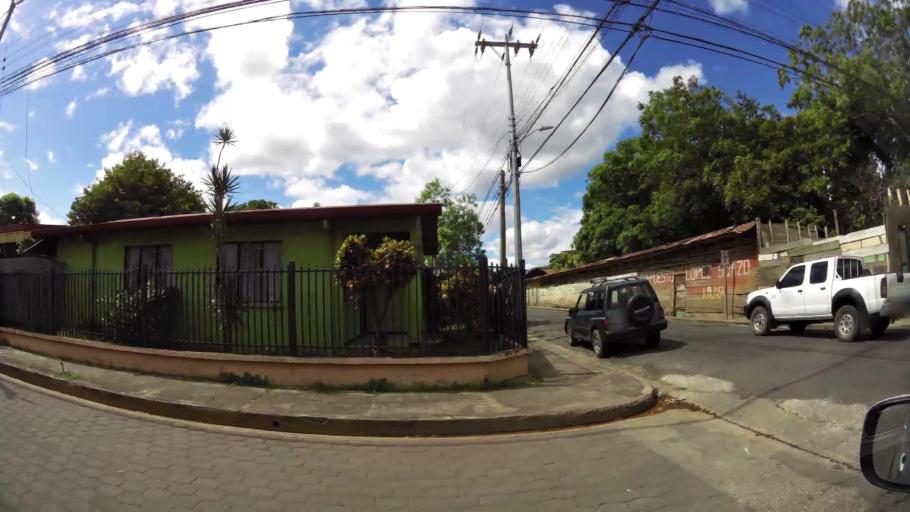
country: CR
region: Guanacaste
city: Santa Cruz
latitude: 10.2606
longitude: -85.5834
